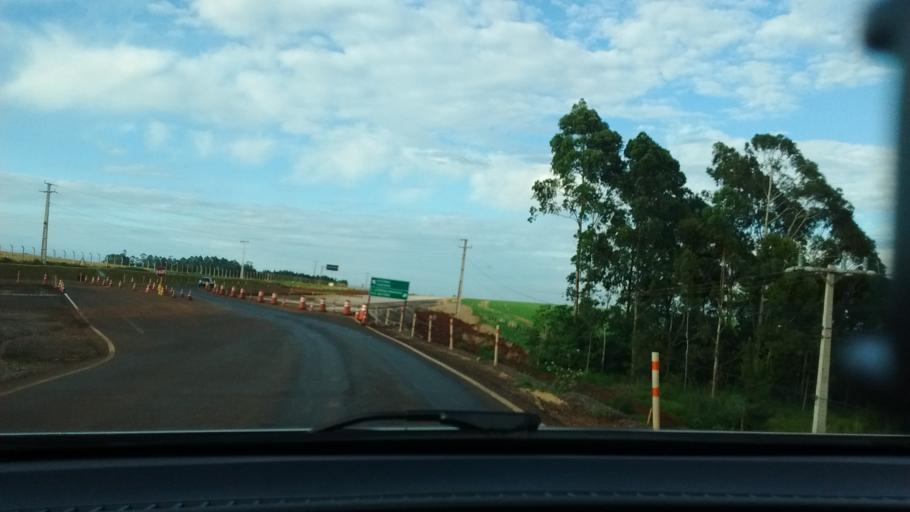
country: BR
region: Parana
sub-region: Cascavel
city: Cascavel
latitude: -25.0814
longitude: -53.5841
